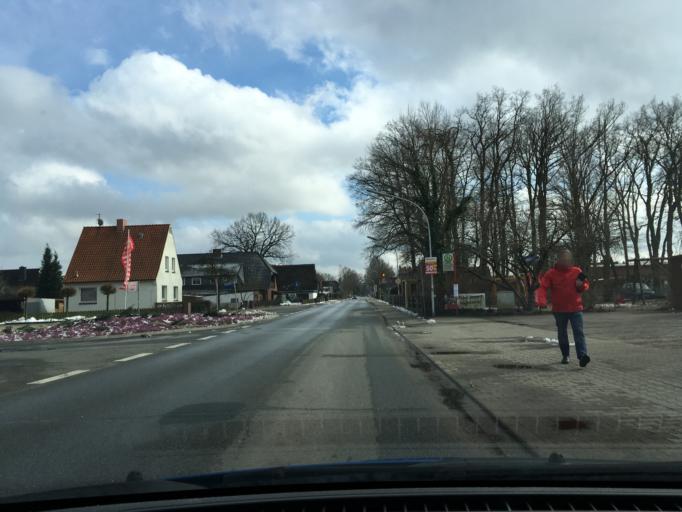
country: DE
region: Lower Saxony
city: Handorf
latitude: 53.3439
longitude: 10.3455
